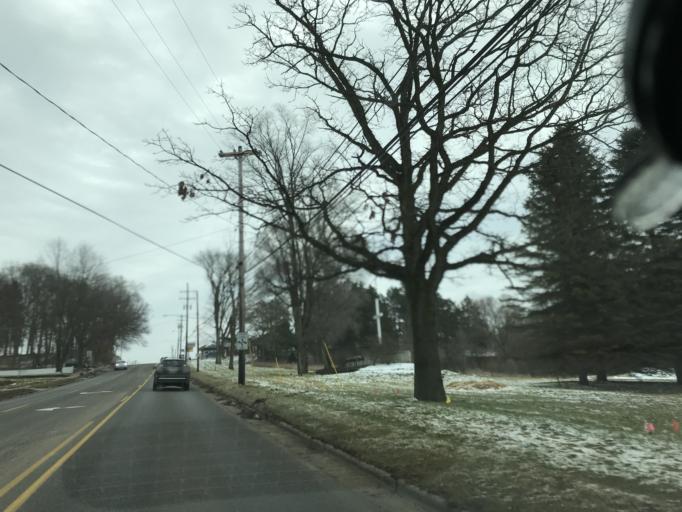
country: US
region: Michigan
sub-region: Kent County
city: Rockford
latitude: 43.1174
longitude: -85.5531
